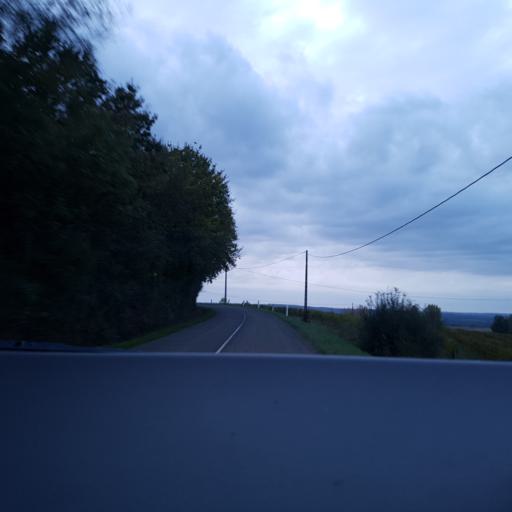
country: FR
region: Midi-Pyrenees
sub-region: Departement du Gers
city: Montreal
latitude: 43.9511
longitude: 0.2590
